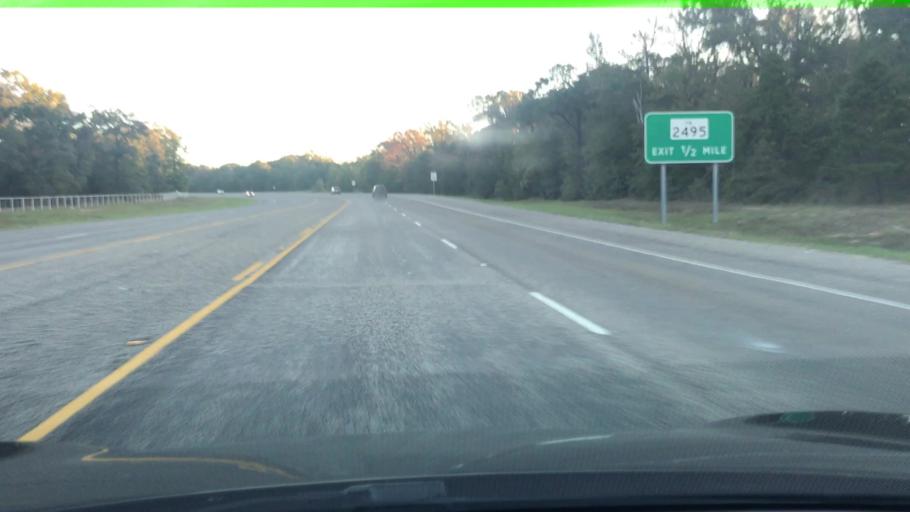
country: US
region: Texas
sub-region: Henderson County
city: Athens
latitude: 32.1961
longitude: -95.8084
